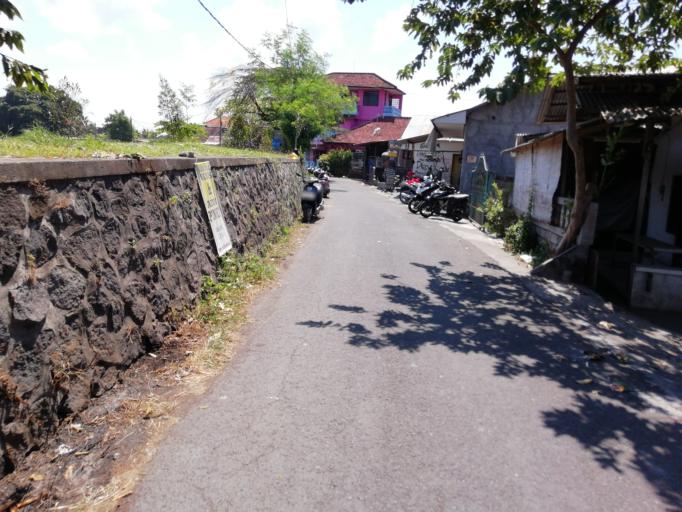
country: ID
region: Bali
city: Karyadharma
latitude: -8.6872
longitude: 115.1990
